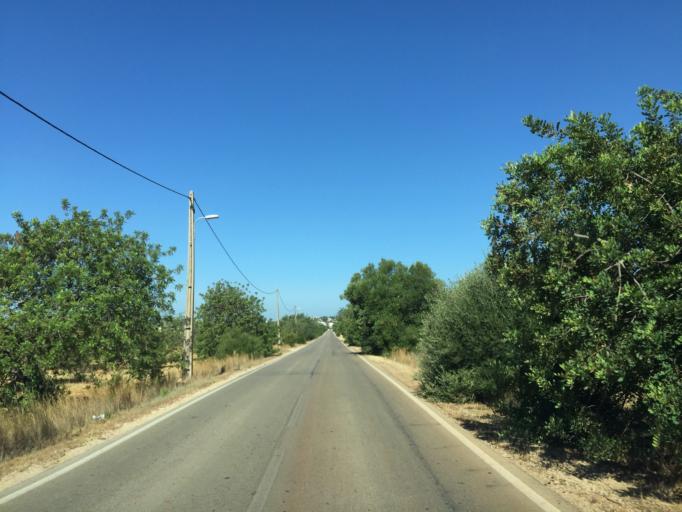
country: PT
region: Faro
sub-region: Loule
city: Almancil
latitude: 37.1095
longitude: -8.0676
